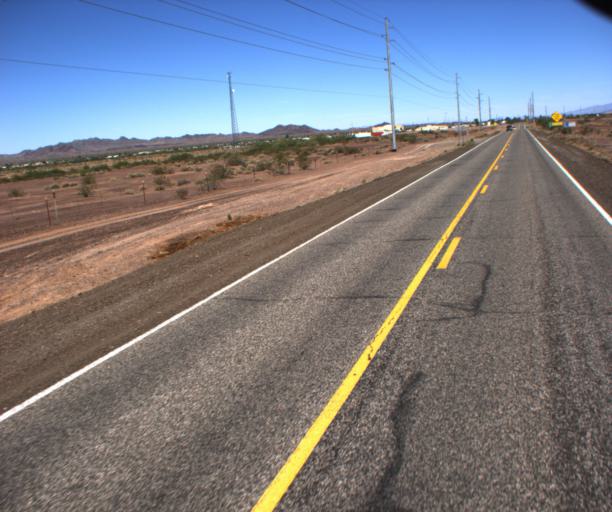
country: US
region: Arizona
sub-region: La Paz County
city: Quartzsite
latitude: 33.9090
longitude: -113.9850
